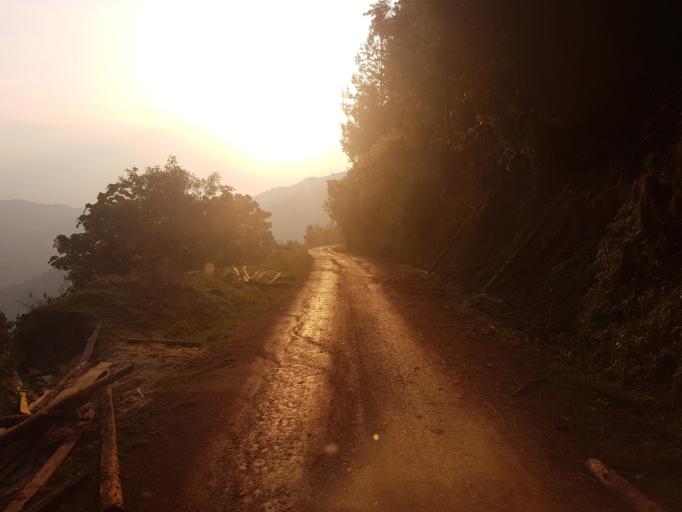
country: UG
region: Western Region
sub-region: Kanungu District
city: Kanungu
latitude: -1.0098
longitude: 29.8491
